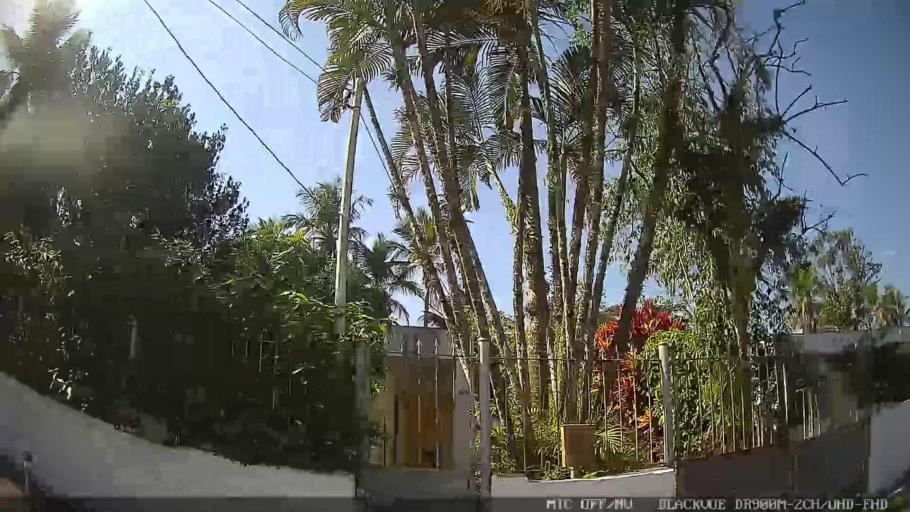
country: BR
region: Sao Paulo
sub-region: Santos
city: Santos
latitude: -23.9360
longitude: -46.3050
